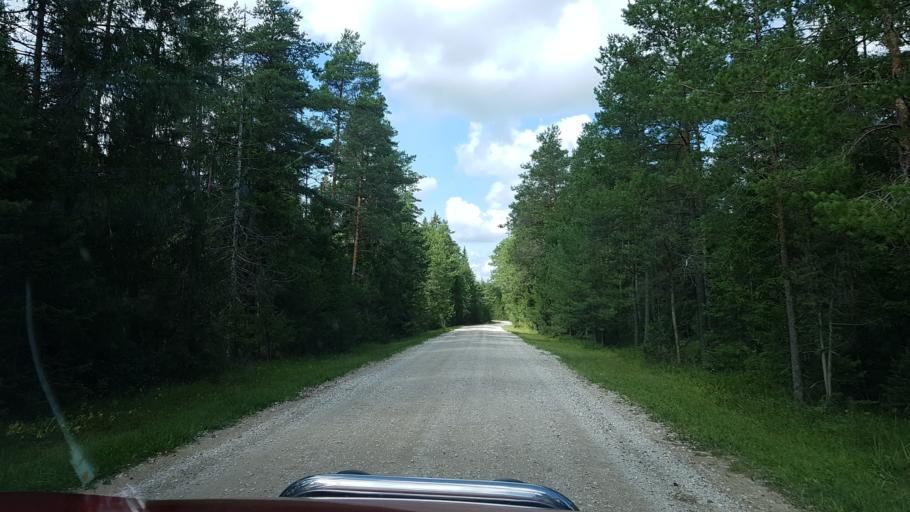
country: EE
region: Raplamaa
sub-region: Rapla vald
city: Rapla
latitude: 58.9567
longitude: 24.6571
